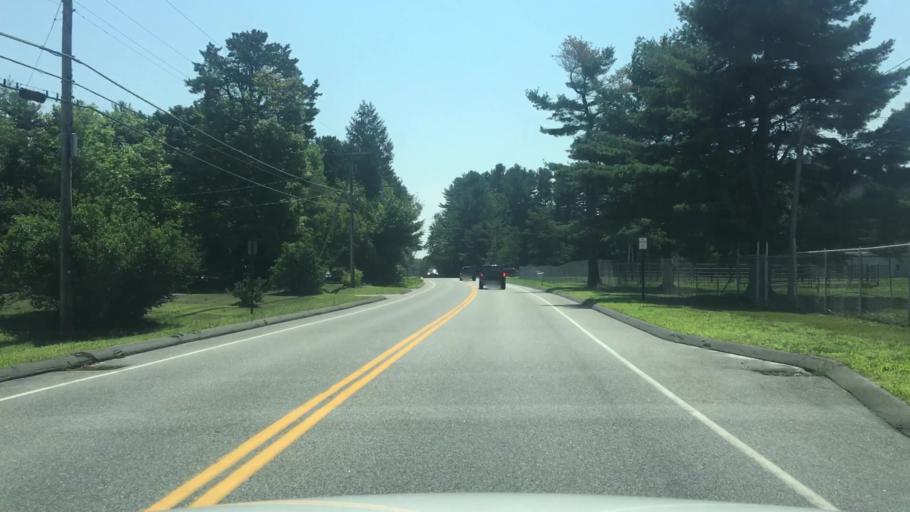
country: US
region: Maine
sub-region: Cumberland County
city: Cumberland Center
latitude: 43.8109
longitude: -70.2871
